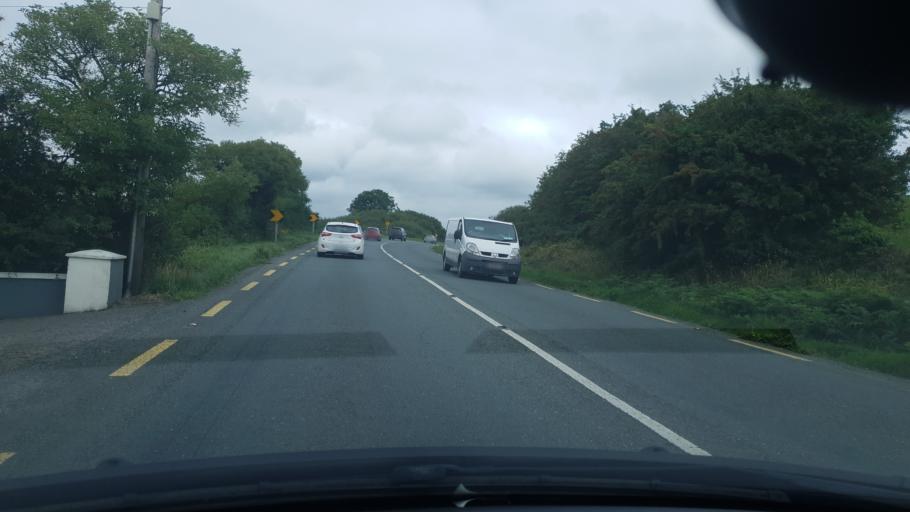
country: IE
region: Munster
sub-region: Ciarrai
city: Cill Airne
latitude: 52.1505
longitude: -9.5546
